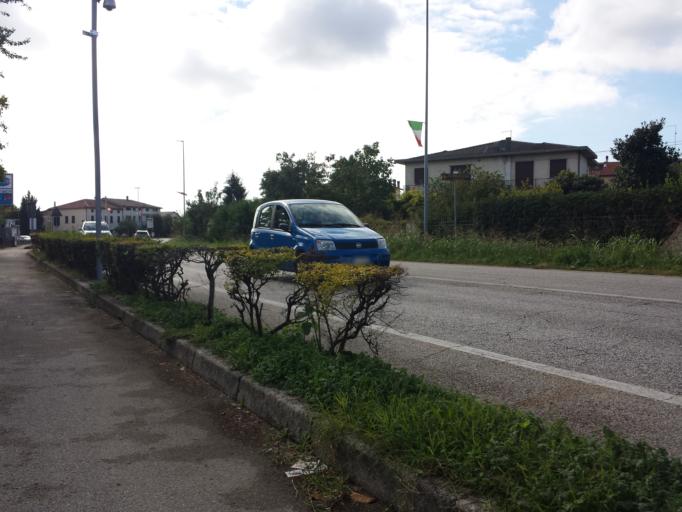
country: IT
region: Veneto
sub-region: Provincia di Vicenza
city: Sandrigo
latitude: 45.6586
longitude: 11.5925
